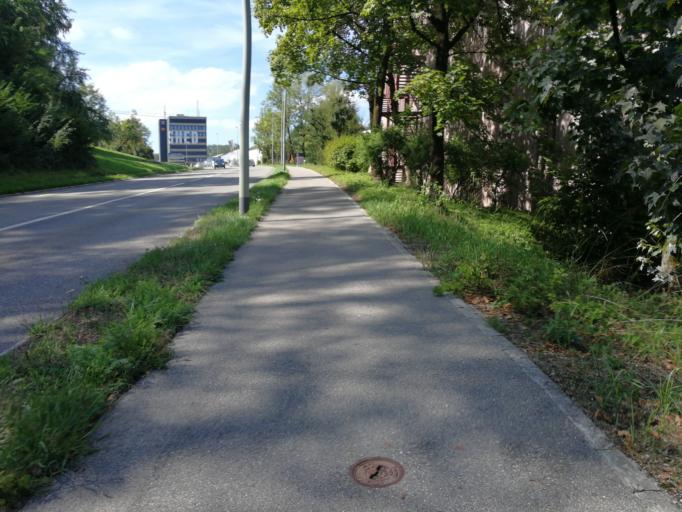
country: CH
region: Zurich
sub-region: Bezirk Horgen
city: Au
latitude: 47.2380
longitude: 8.6419
